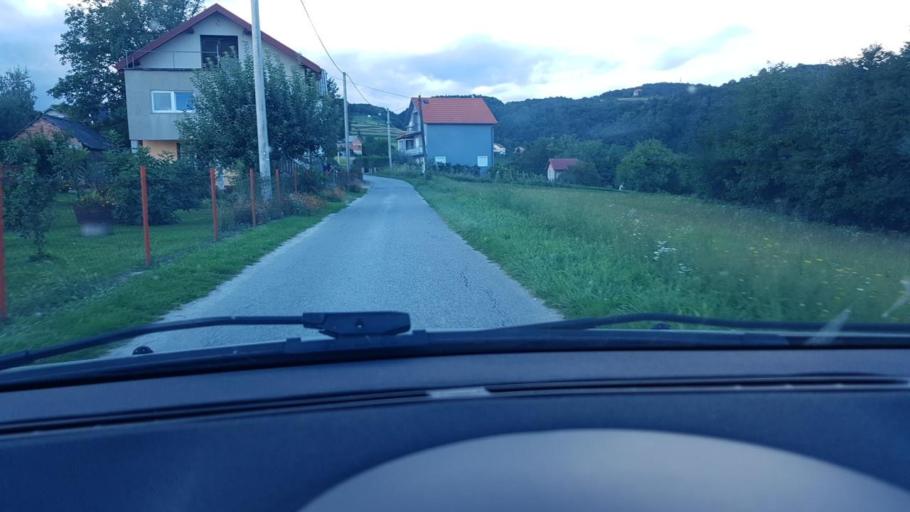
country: HR
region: Krapinsko-Zagorska
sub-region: Grad Krapina
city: Krapina
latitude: 46.1666
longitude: 15.8278
